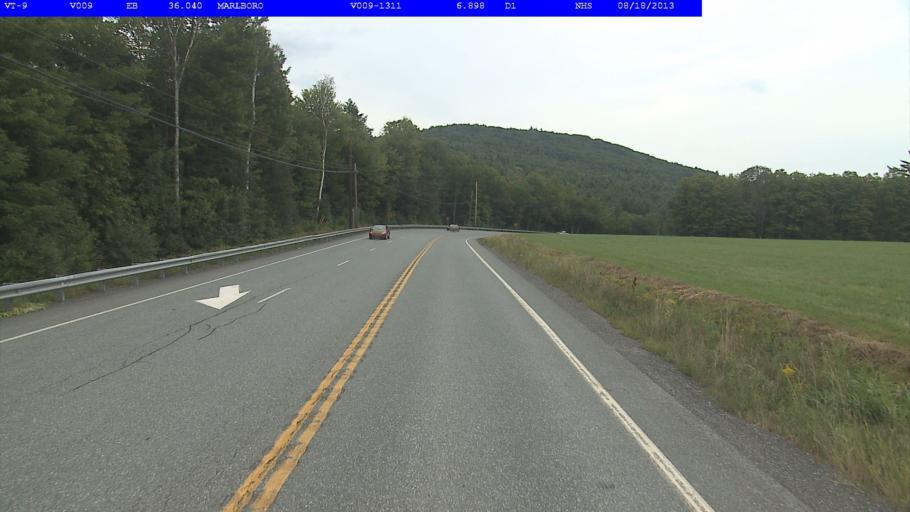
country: US
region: Vermont
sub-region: Windham County
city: West Brattleboro
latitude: 42.8798
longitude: -72.7018
